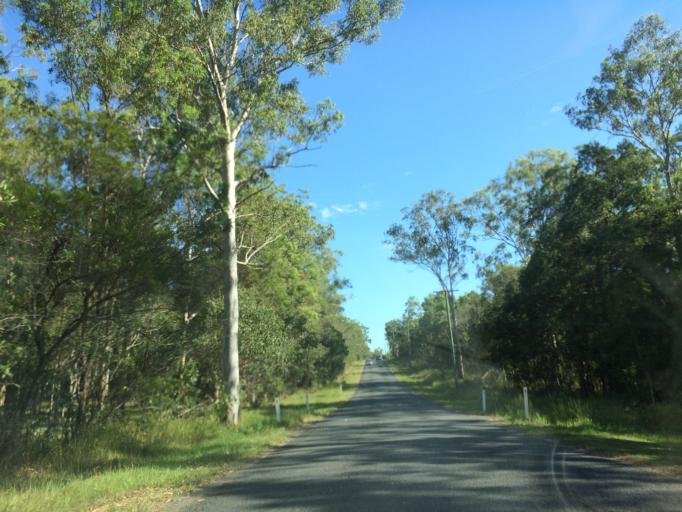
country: AU
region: Queensland
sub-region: Ipswich
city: Springfield Lakes
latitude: -27.7085
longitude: 152.9568
